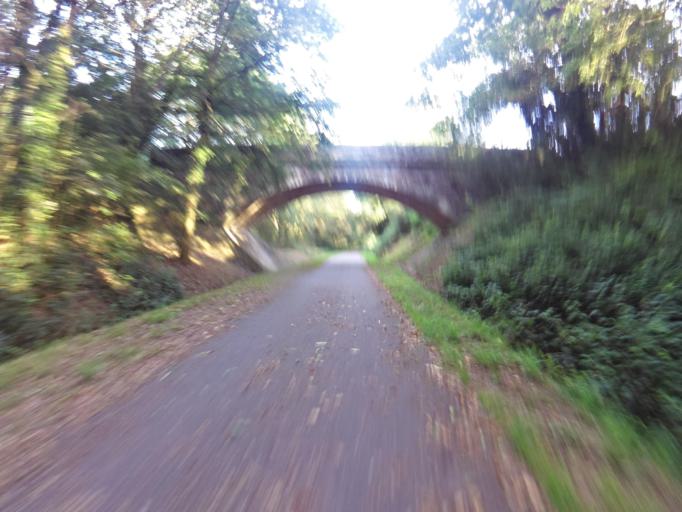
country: FR
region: Brittany
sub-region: Departement du Morbihan
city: Malestroit
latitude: 47.8314
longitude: -2.4202
